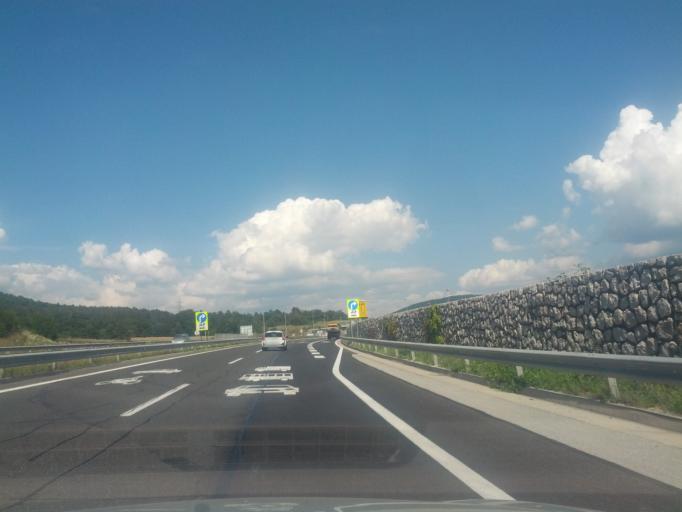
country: SI
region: Hrpelje-Kozina
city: Kozina
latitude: 45.6118
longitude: 13.9335
